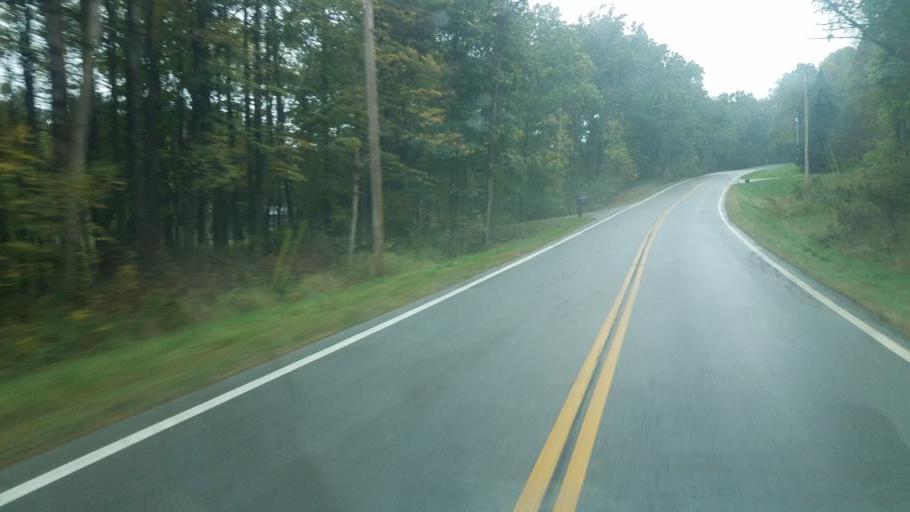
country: US
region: Ohio
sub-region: Sandusky County
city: Bellville
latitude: 40.5880
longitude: -82.3868
